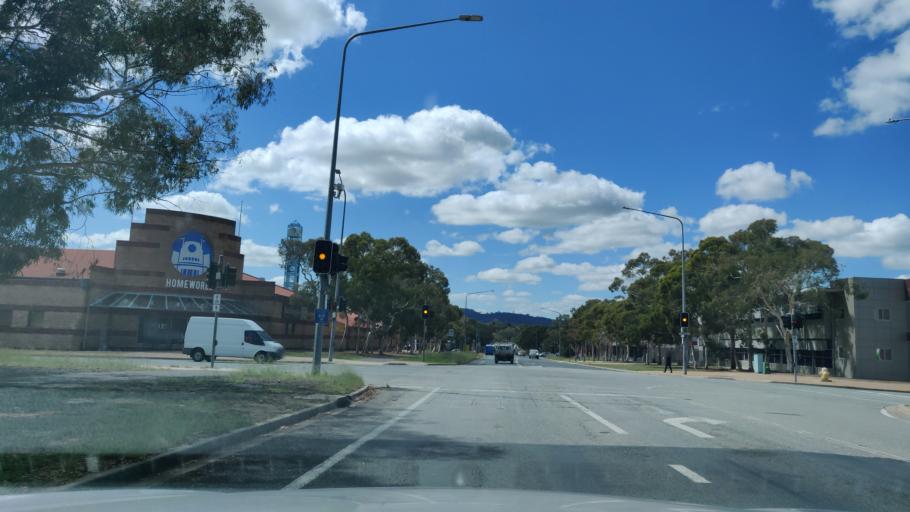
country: AU
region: Australian Capital Territory
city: Macarthur
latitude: -35.4193
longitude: 149.0668
